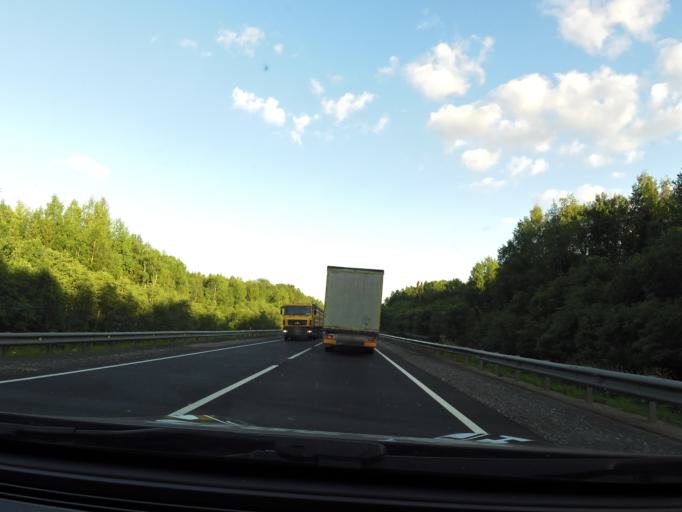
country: RU
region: Vologda
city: Gryazovets
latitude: 58.9627
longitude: 40.1604
